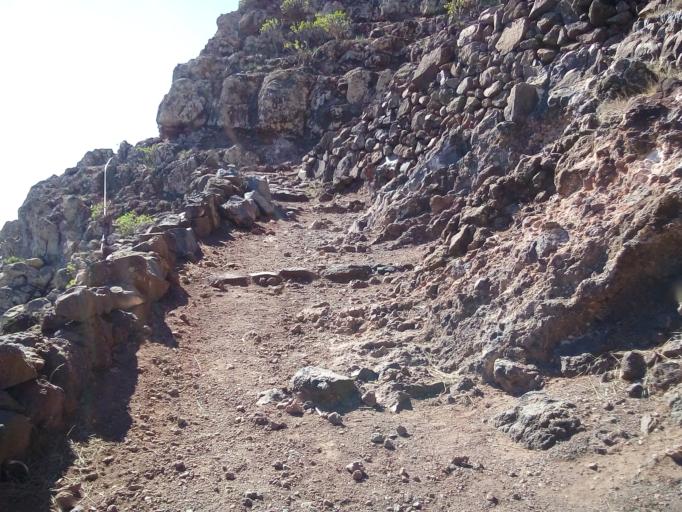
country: ES
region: Canary Islands
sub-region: Provincia de Santa Cruz de Tenerife
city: Vallehermosa
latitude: 28.1176
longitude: -17.3350
